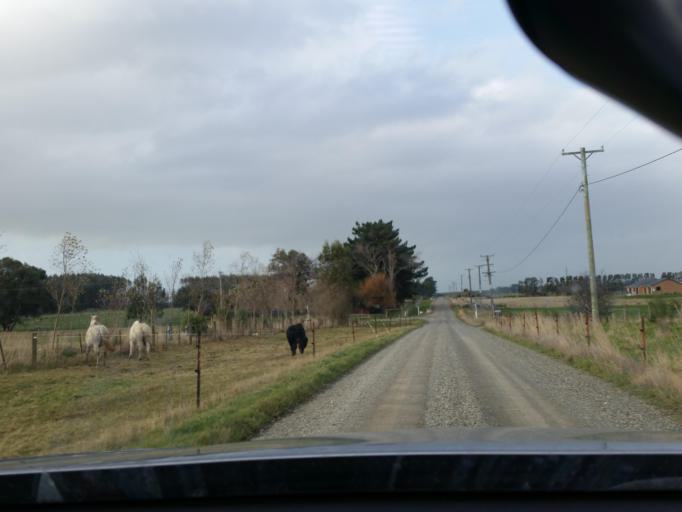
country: NZ
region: Southland
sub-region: Invercargill City
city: Invercargill
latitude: -46.3366
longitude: 168.3734
